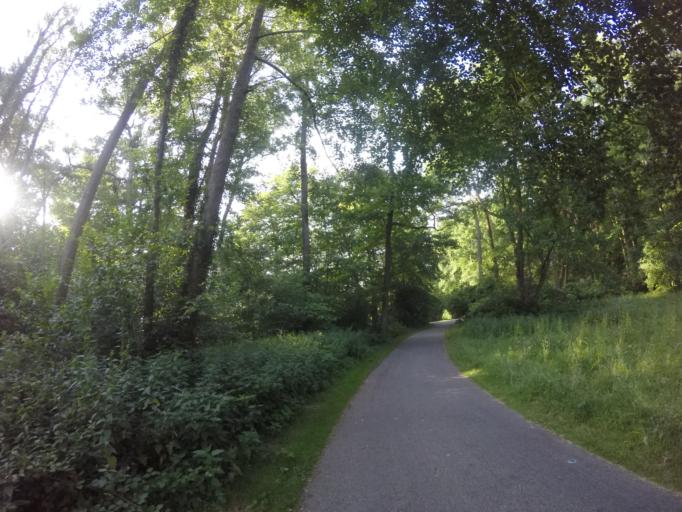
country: NL
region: Gelderland
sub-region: Gemeente Arnhem
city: Burgemeesterswijk
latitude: 51.9929
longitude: 5.8997
